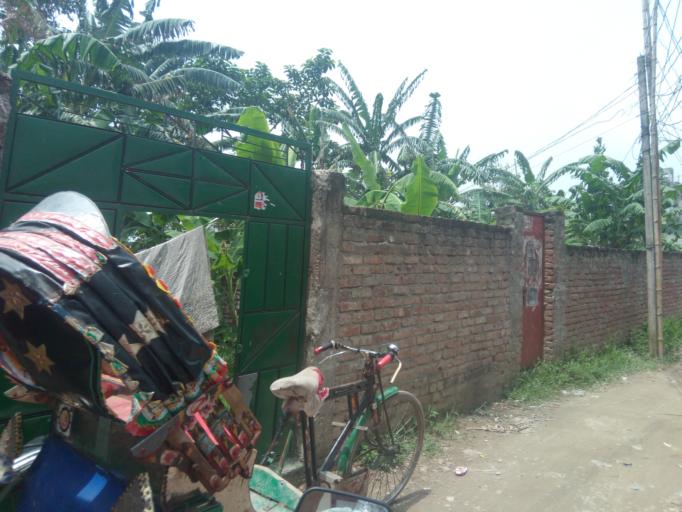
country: BD
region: Dhaka
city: Paltan
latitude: 23.7556
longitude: 90.4303
